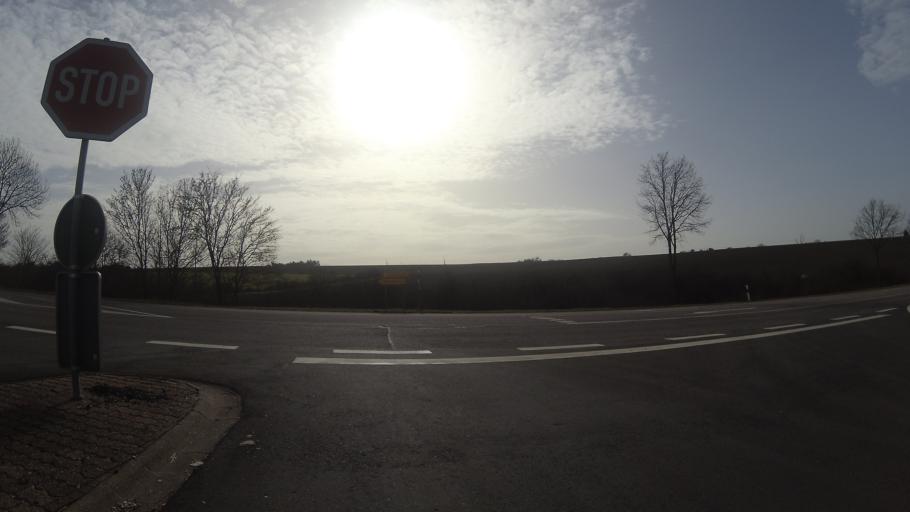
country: FR
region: Lorraine
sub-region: Departement de la Moselle
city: Merten
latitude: 49.2975
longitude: 6.6700
